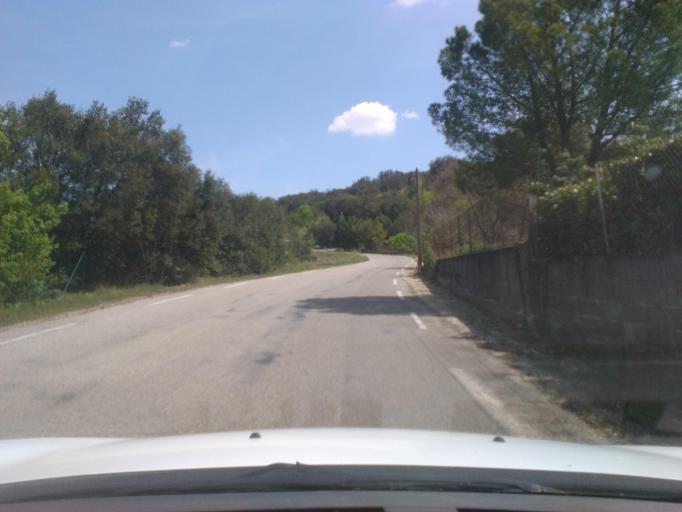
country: FR
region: Languedoc-Roussillon
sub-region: Departement du Gard
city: Saint-Hippolyte-du-Fort
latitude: 43.9687
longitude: 3.8720
